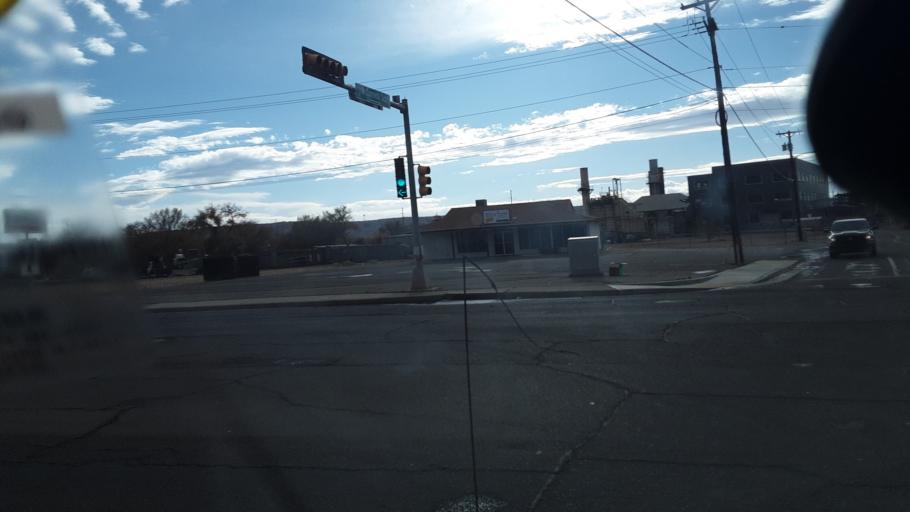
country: US
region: New Mexico
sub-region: San Juan County
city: Farmington
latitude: 36.7262
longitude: -108.1898
